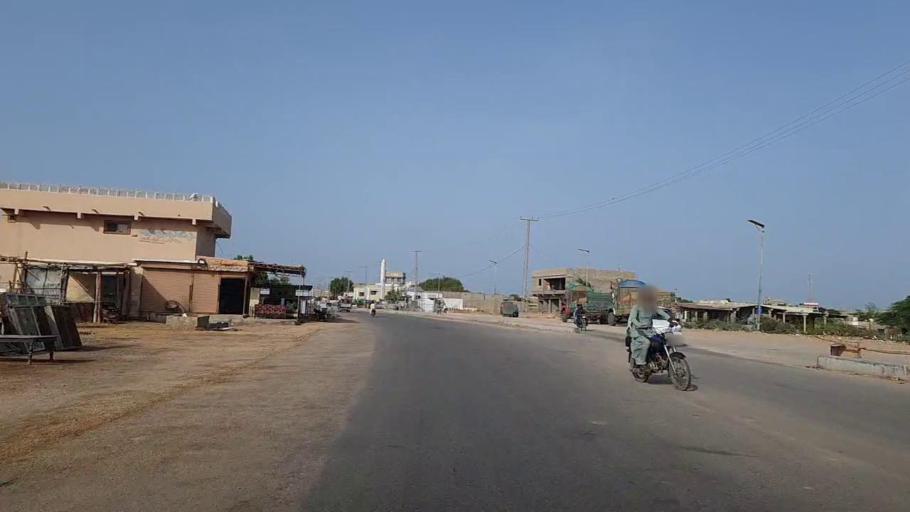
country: PK
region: Sindh
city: Thatta
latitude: 24.7488
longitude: 67.9148
